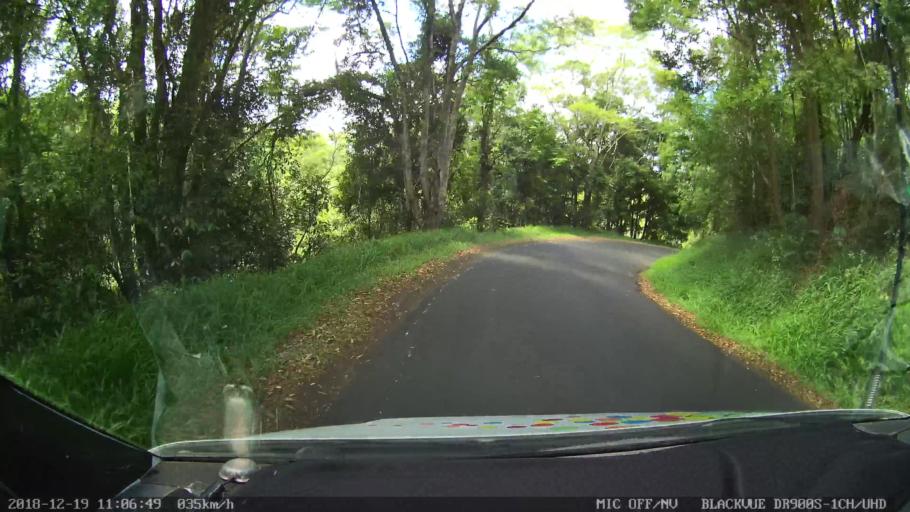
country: AU
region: New South Wales
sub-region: Lismore Municipality
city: Nimbin
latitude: -28.6238
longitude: 153.2679
